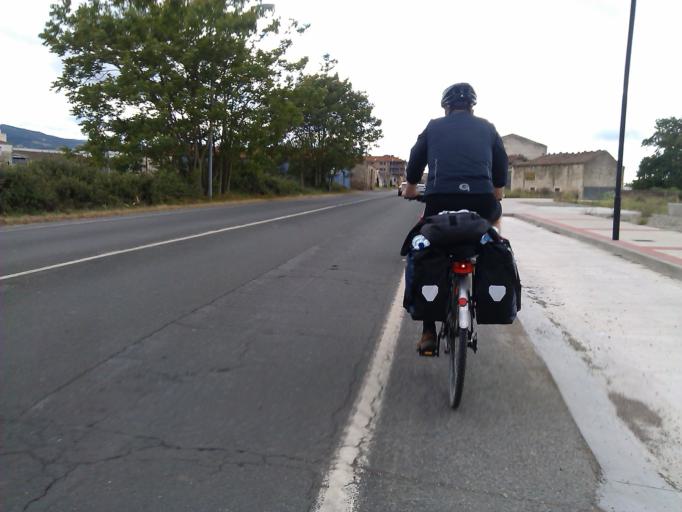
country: ES
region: La Rioja
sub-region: Provincia de La Rioja
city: Santo Domingo de la Calzada
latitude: 42.4392
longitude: -2.9413
